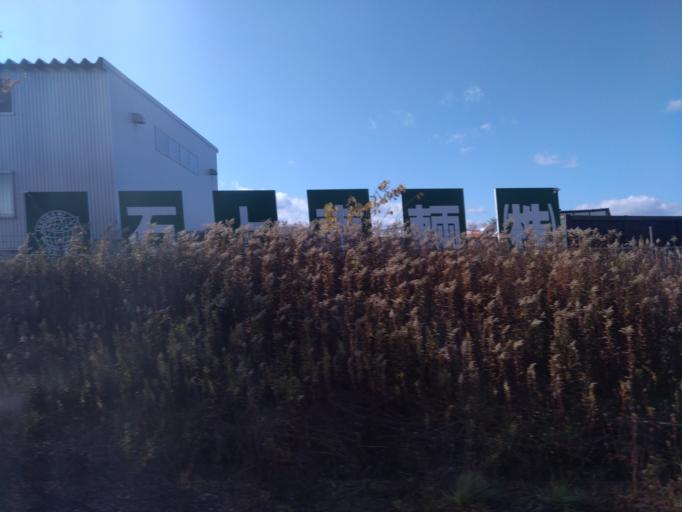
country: JP
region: Hokkaido
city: Kitahiroshima
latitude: 42.9286
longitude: 141.5728
